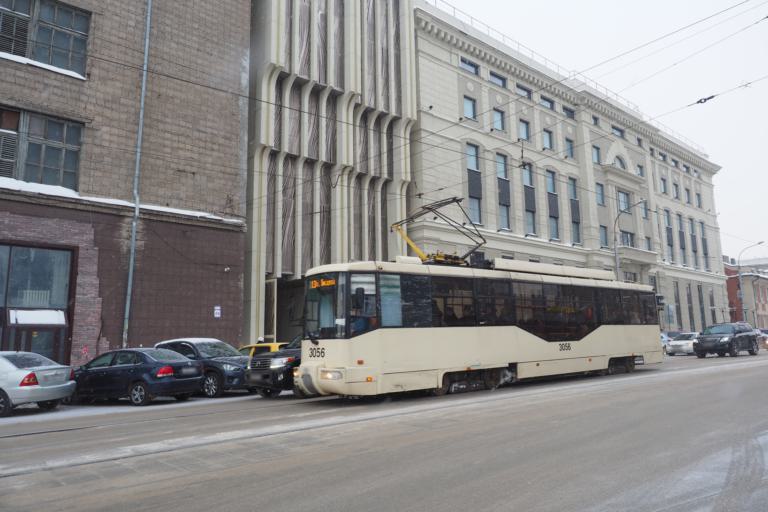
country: RU
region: Novosibirsk
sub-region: Novosibirskiy Rayon
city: Novosibirsk
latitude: 55.0264
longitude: 82.9256
